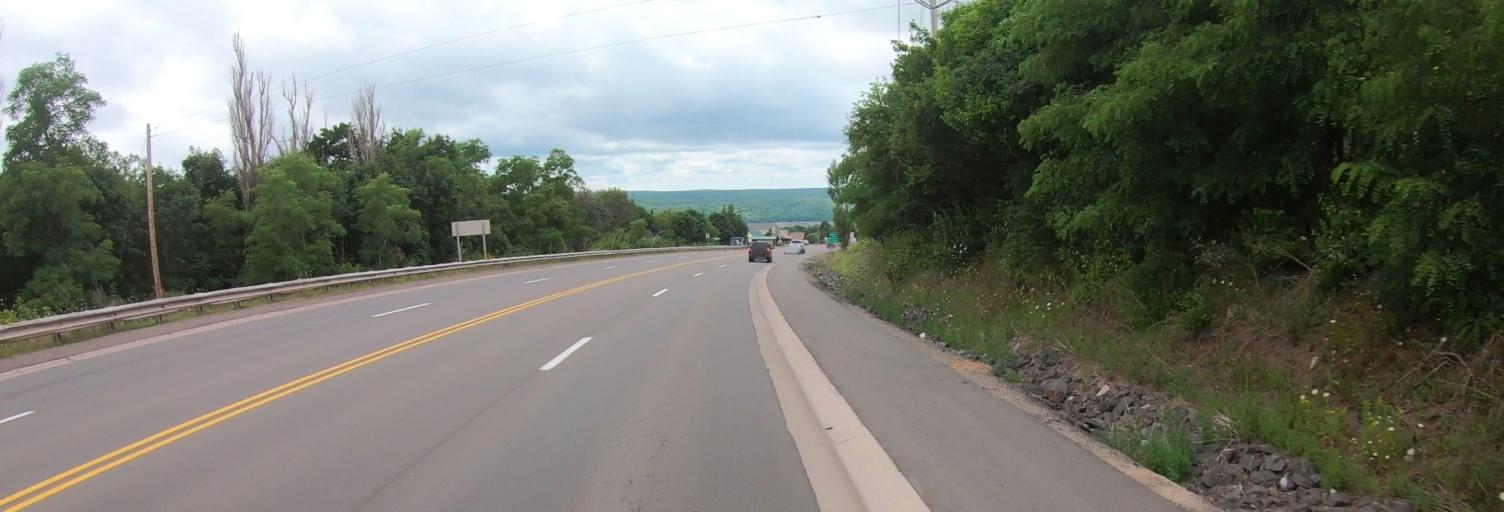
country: US
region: Michigan
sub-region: Houghton County
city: Hancock
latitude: 47.1308
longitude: -88.5835
